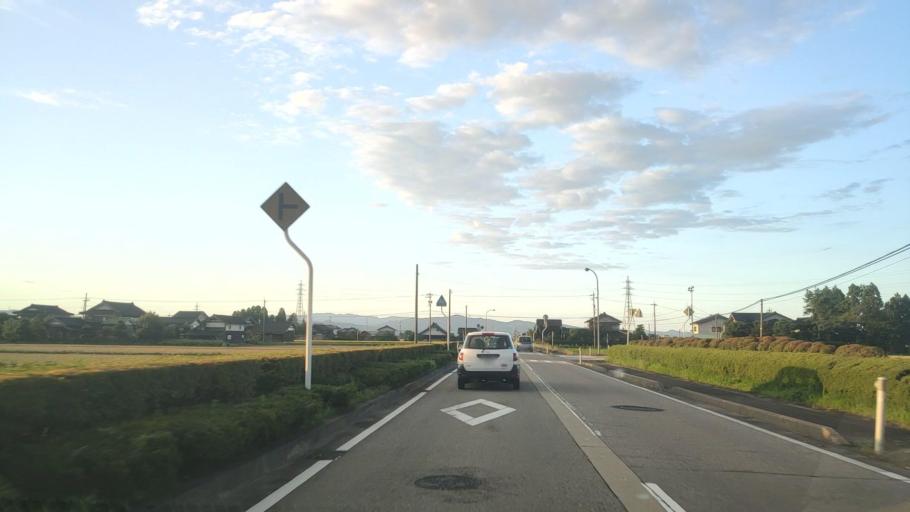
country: JP
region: Toyama
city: Nanto-shi
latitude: 36.6170
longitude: 136.8895
